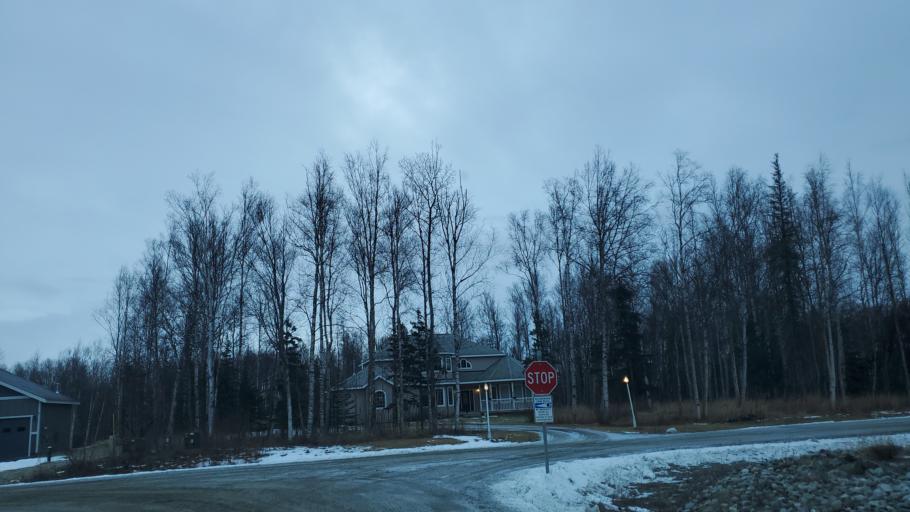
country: US
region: Alaska
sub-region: Matanuska-Susitna Borough
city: Farm Loop
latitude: 61.6522
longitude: -149.2214
